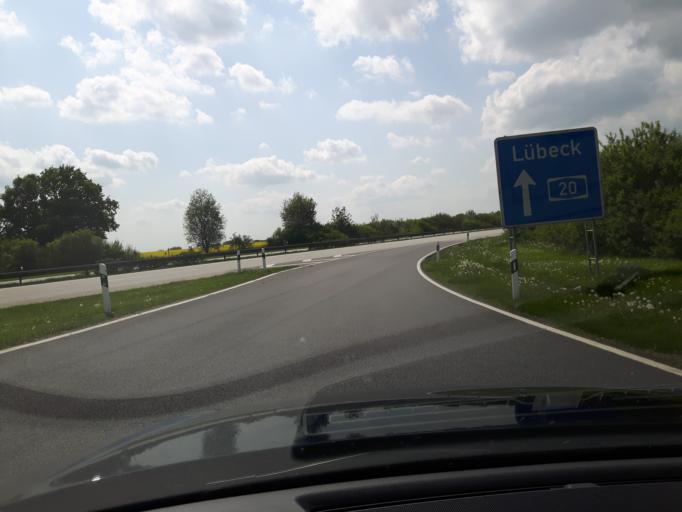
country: DE
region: Mecklenburg-Vorpommern
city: Grevesmuhlen
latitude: 53.8273
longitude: 11.2507
